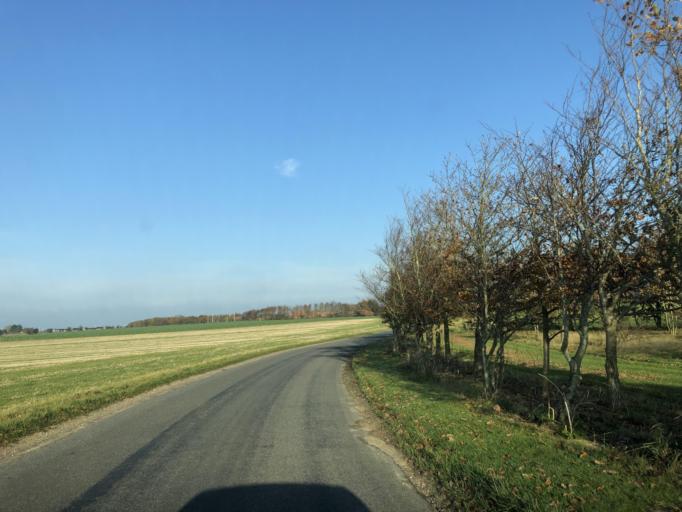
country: DK
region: Central Jutland
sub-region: Holstebro Kommune
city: Vinderup
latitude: 56.3989
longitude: 8.7468
